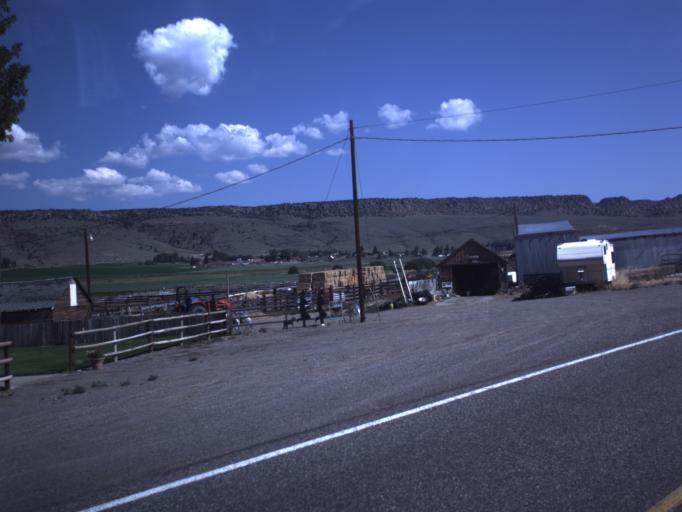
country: US
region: Utah
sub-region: Wayne County
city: Loa
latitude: 38.4381
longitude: -111.6195
